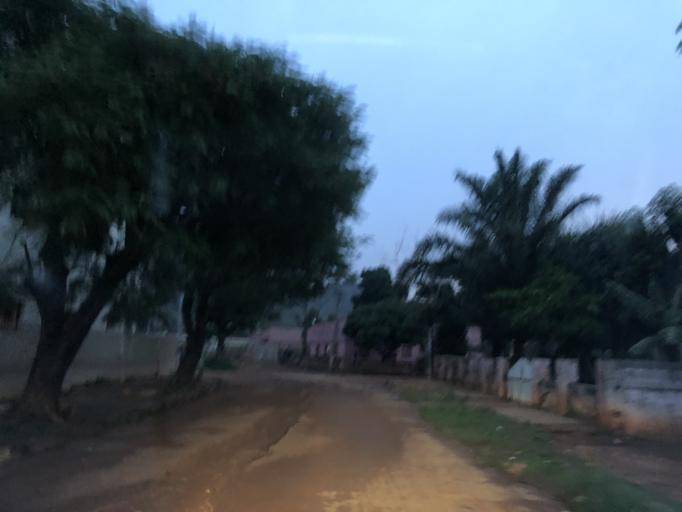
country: AO
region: Cuanza Sul
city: Uacu Cungo
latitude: -11.3637
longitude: 15.1143
